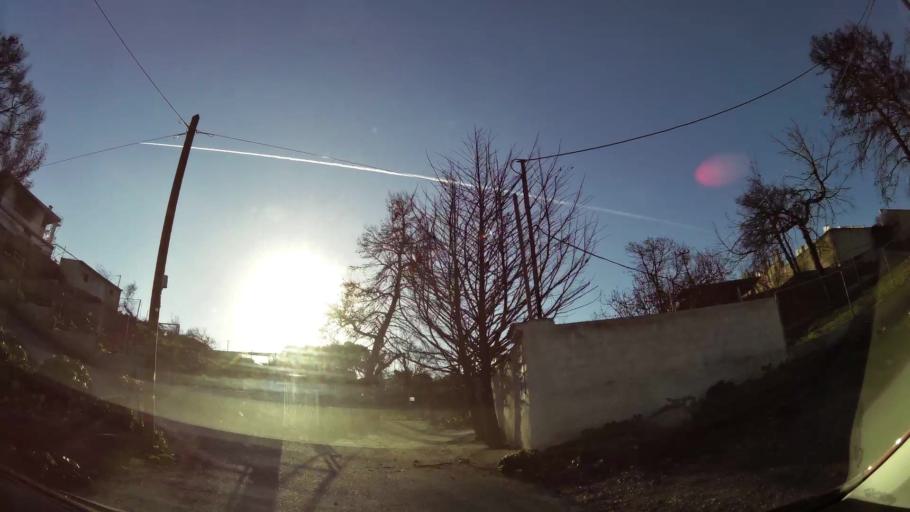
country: GR
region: Attica
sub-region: Nomarchia Anatolikis Attikis
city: Rafina
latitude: 38.0314
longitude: 23.9988
